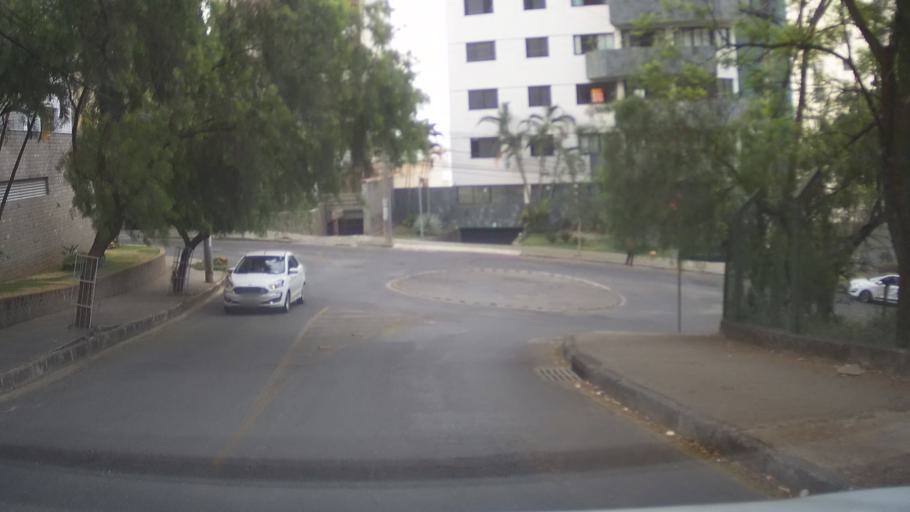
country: BR
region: Minas Gerais
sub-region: Belo Horizonte
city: Belo Horizonte
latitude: -19.8946
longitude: -43.9294
